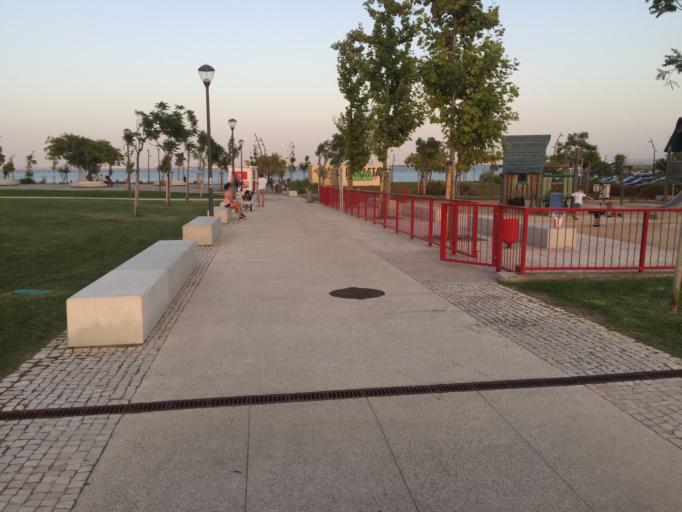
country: PT
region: Lisbon
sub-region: Loures
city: Moscavide
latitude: 38.7433
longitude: -9.0989
